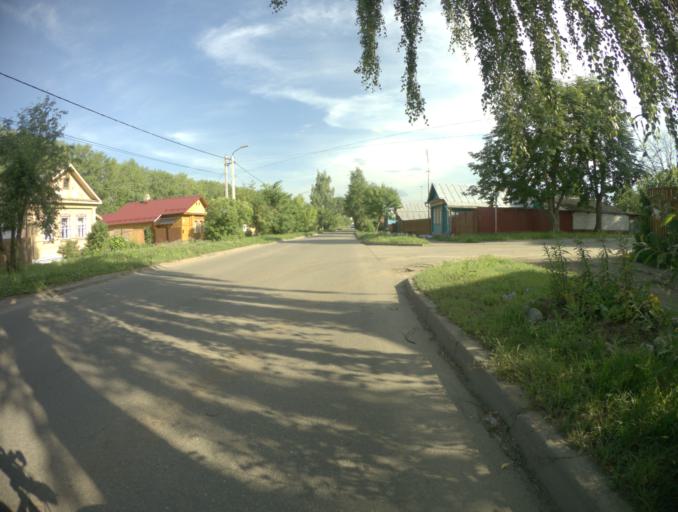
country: RU
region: Vladimir
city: Suzdal'
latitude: 56.4250
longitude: 40.4564
